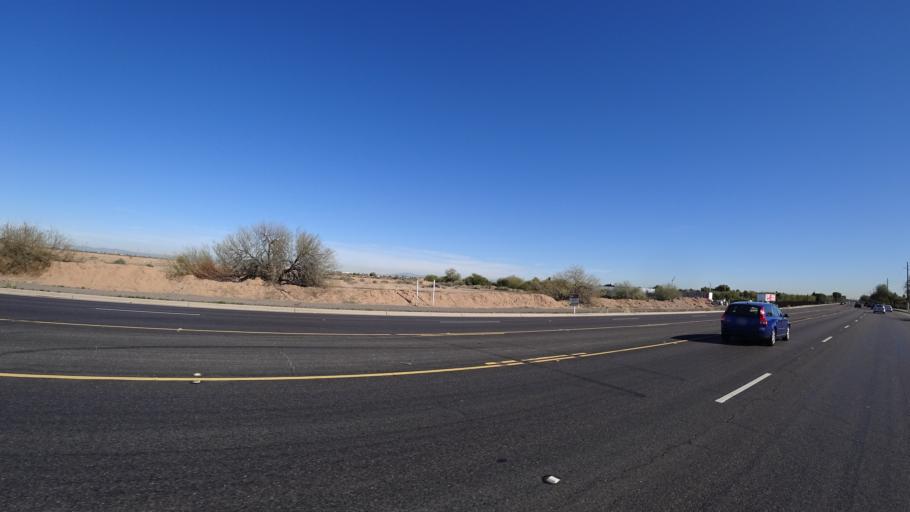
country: US
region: Arizona
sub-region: Maricopa County
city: Litchfield Park
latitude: 33.4930
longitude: -112.3078
